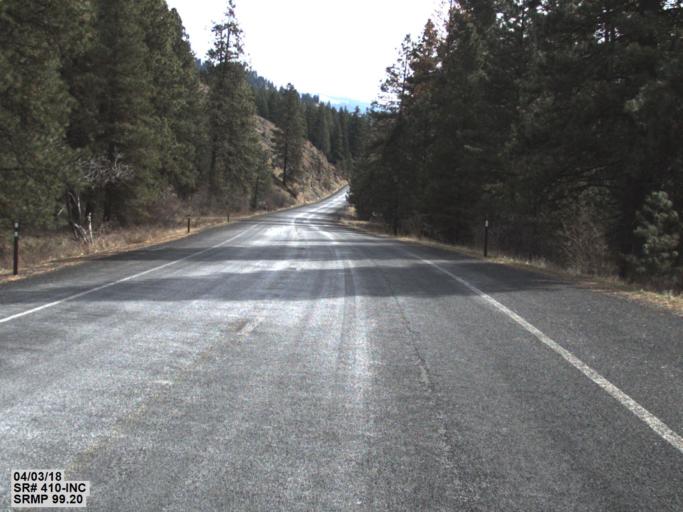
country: US
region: Washington
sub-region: Kittitas County
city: Cle Elum
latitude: 46.9085
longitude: -121.0279
